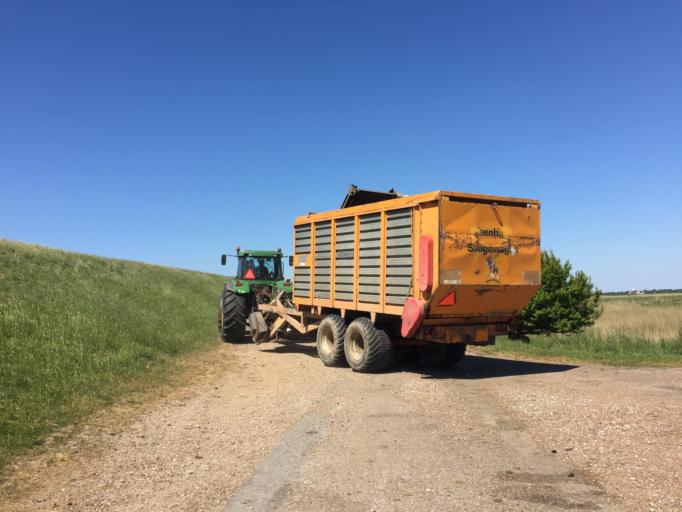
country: DK
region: South Denmark
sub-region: Esbjerg Kommune
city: Ribe
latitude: 55.2681
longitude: 8.6620
